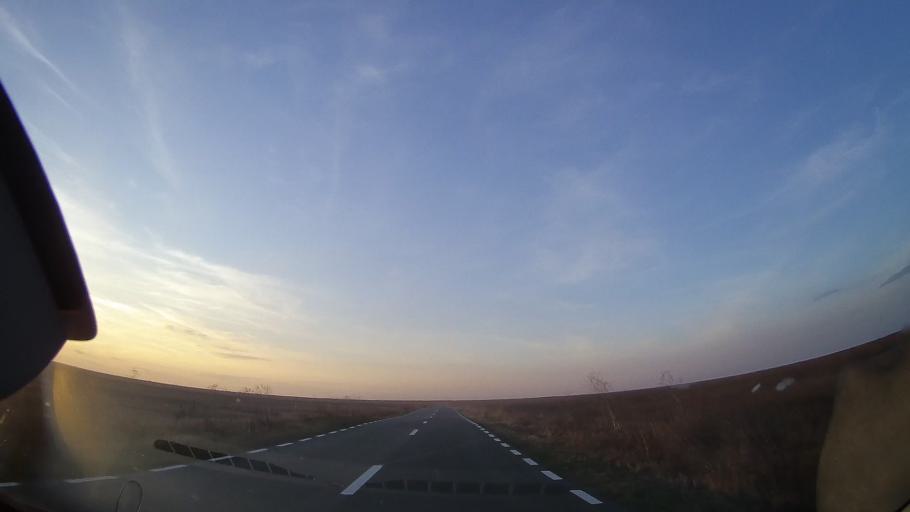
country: RO
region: Constanta
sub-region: Comuna Topraisar
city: Topraisar
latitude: 44.0144
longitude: 28.4351
